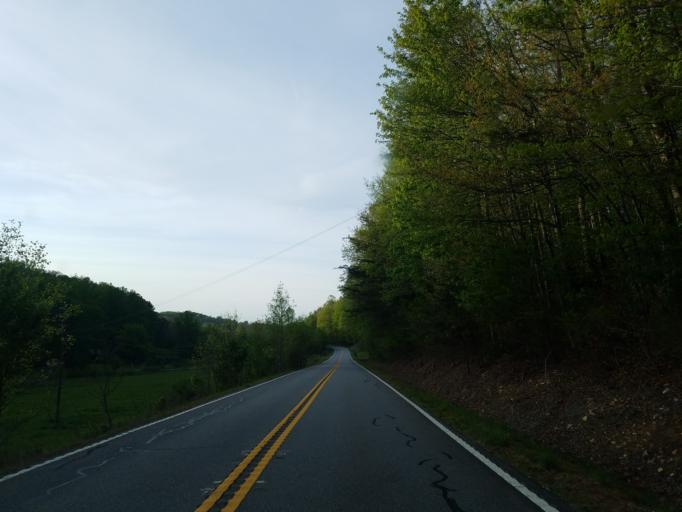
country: US
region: Georgia
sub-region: Fannin County
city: Blue Ridge
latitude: 34.8221
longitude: -84.1890
